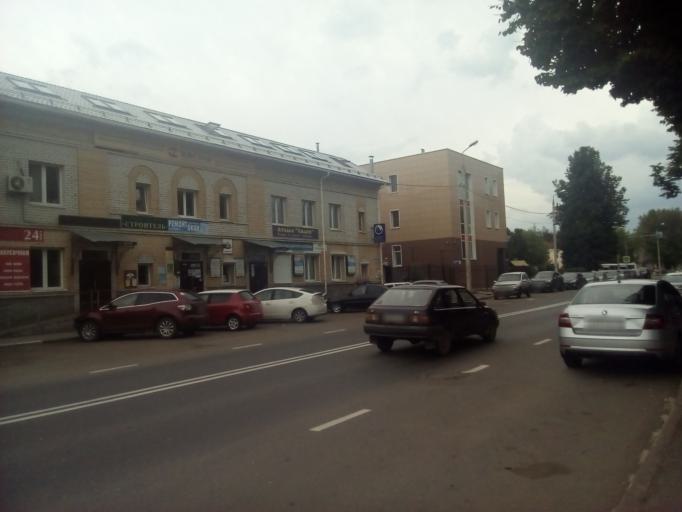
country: RU
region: Jaroslavl
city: Yaroslavl
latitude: 57.6102
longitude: 39.8761
